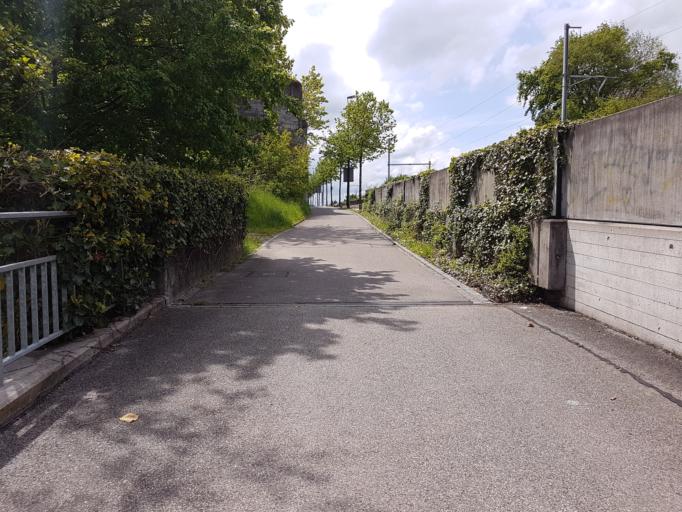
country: CH
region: Aargau
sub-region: Bezirk Zurzach
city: Klingnau
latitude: 47.5677
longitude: 8.2568
